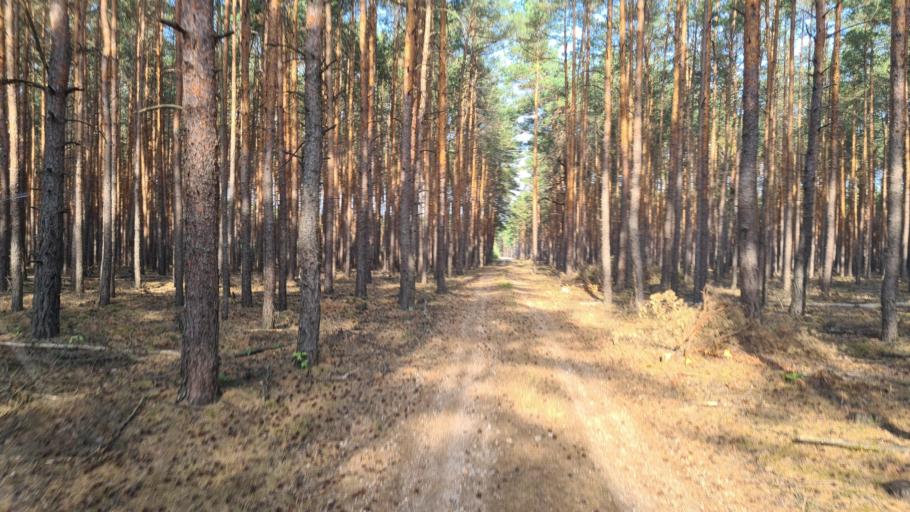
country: DE
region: Brandenburg
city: Crinitz
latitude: 51.6729
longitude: 13.7749
